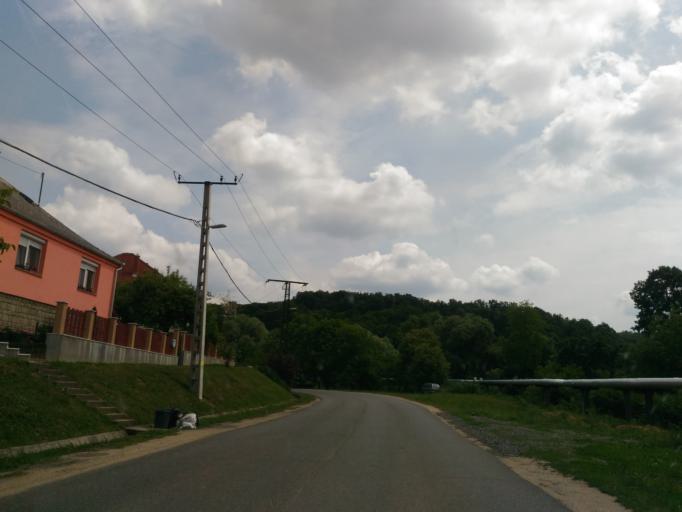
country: HU
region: Baranya
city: Komlo
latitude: 46.1859
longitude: 18.2428
